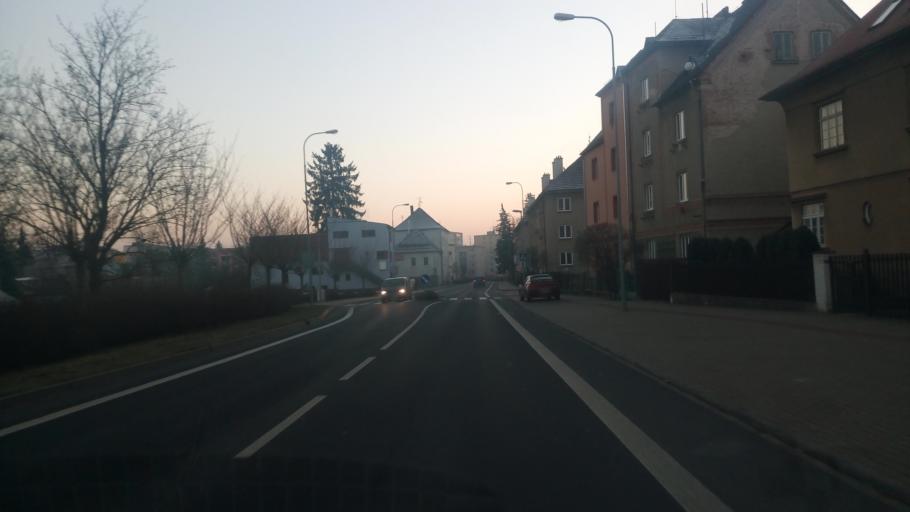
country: CZ
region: Olomoucky
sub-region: Okres Sumperk
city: Sumperk
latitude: 49.9739
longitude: 16.9739
